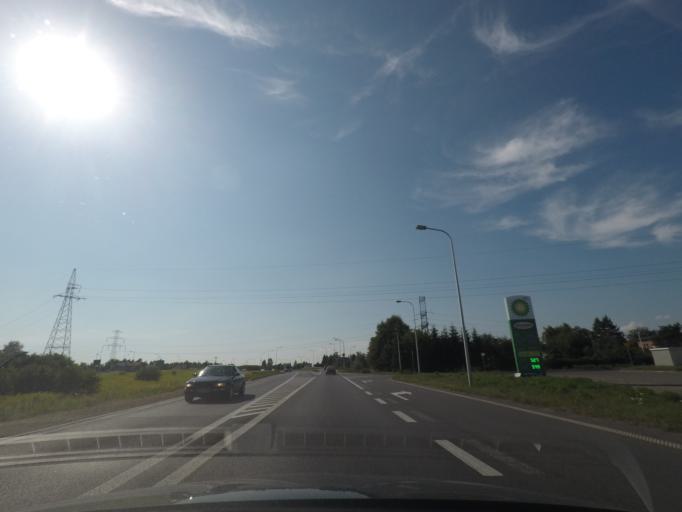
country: PL
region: Silesian Voivodeship
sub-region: Zory
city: Zory
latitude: 50.0610
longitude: 18.6665
